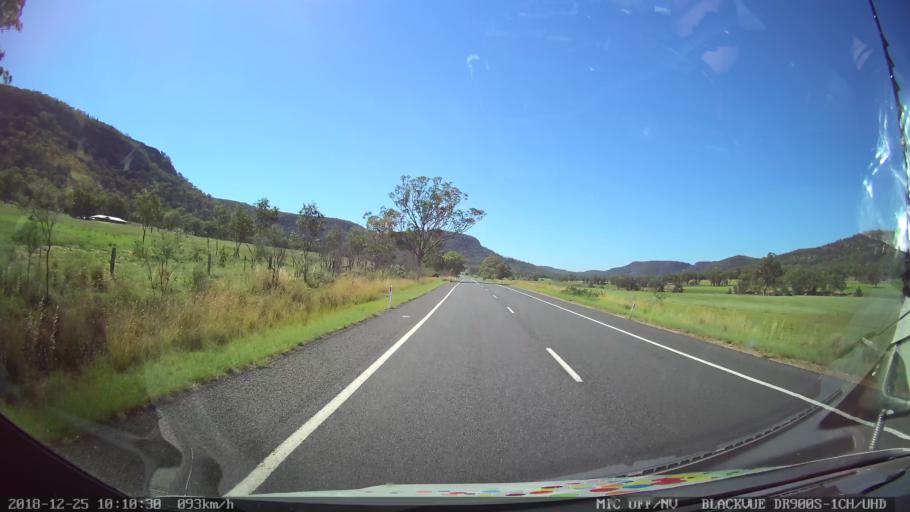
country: AU
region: New South Wales
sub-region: Muswellbrook
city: Denman
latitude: -32.3044
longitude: 150.5225
